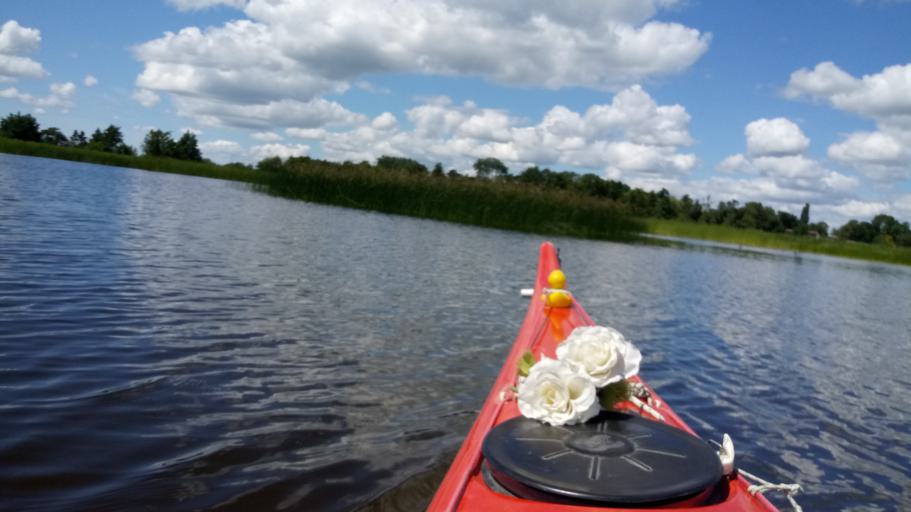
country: NL
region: Overijssel
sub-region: Gemeente Steenwijkerland
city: Giethoorn
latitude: 52.7049
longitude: 6.0809
